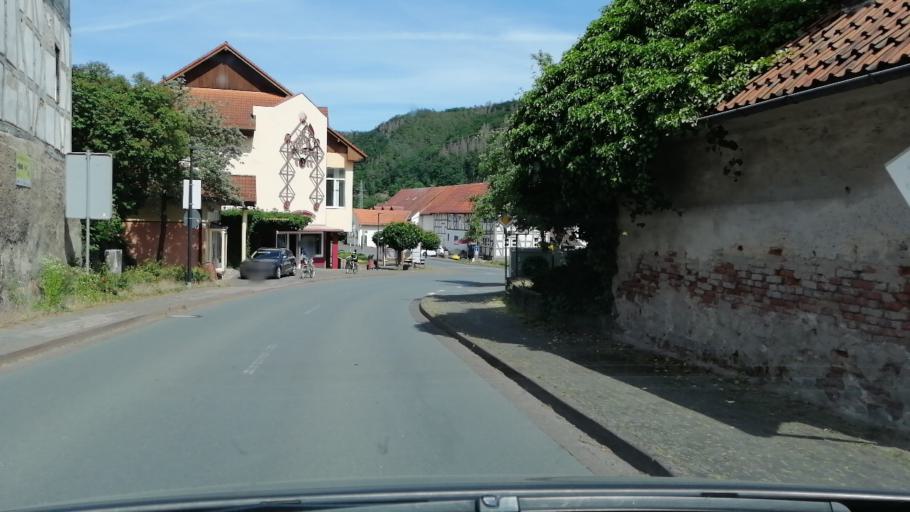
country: DE
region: Hesse
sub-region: Regierungsbezirk Kassel
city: Waldeck
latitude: 51.1719
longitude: 9.0520
